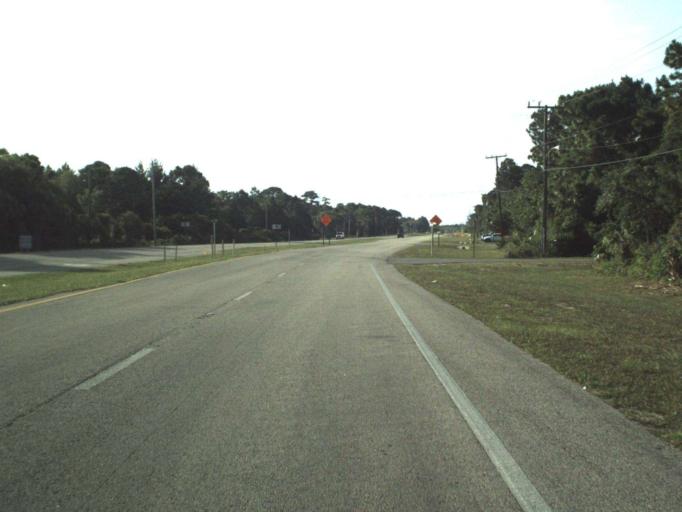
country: US
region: Florida
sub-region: Volusia County
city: Edgewater
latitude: 28.9396
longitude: -80.8809
